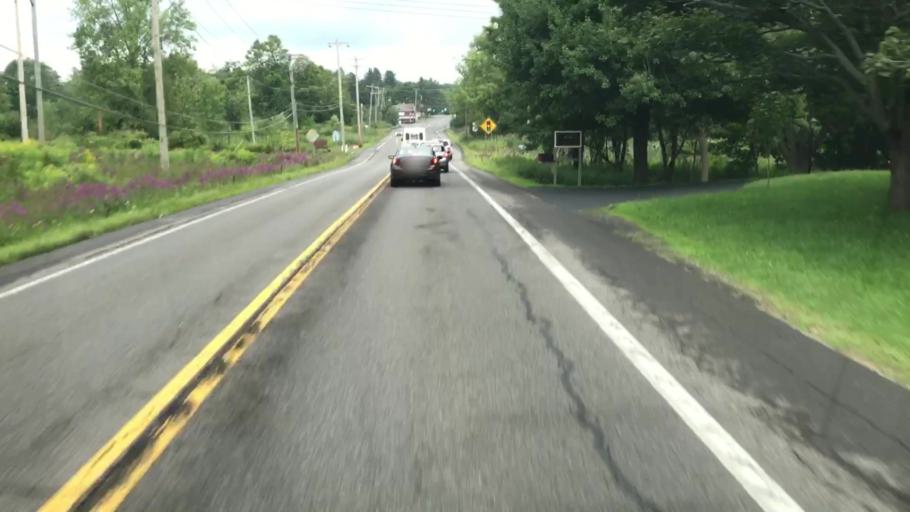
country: US
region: New York
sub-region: Onondaga County
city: Liverpool
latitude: 43.1831
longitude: -76.2166
